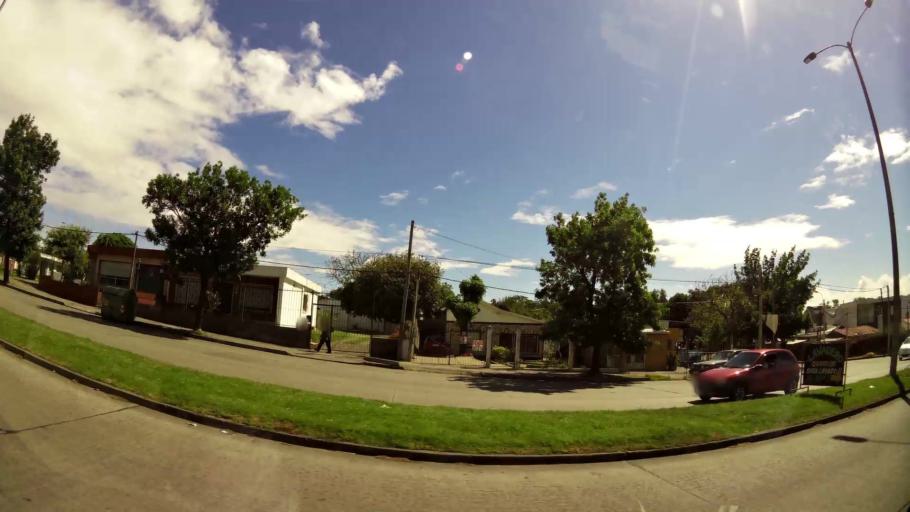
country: UY
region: Montevideo
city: Montevideo
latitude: -34.8492
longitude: -56.1866
